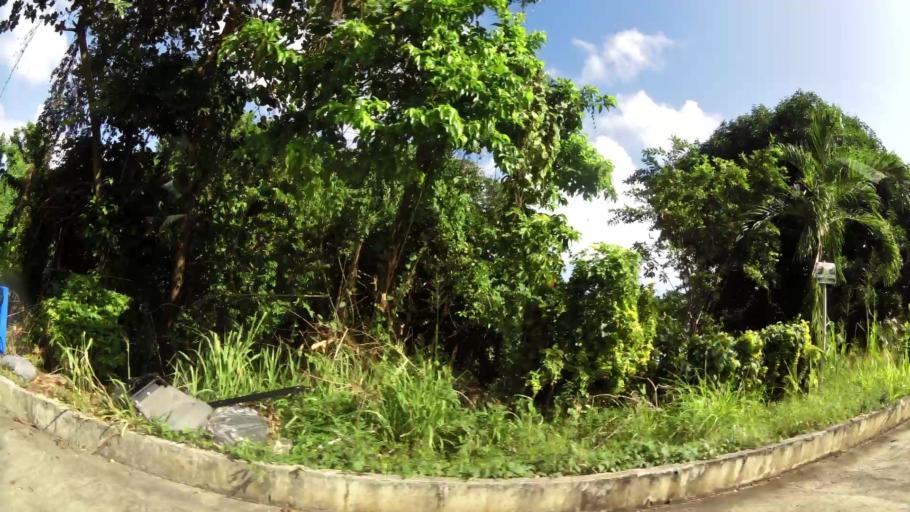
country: MQ
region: Martinique
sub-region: Martinique
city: Sainte-Marie
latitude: 14.7952
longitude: -61.0033
